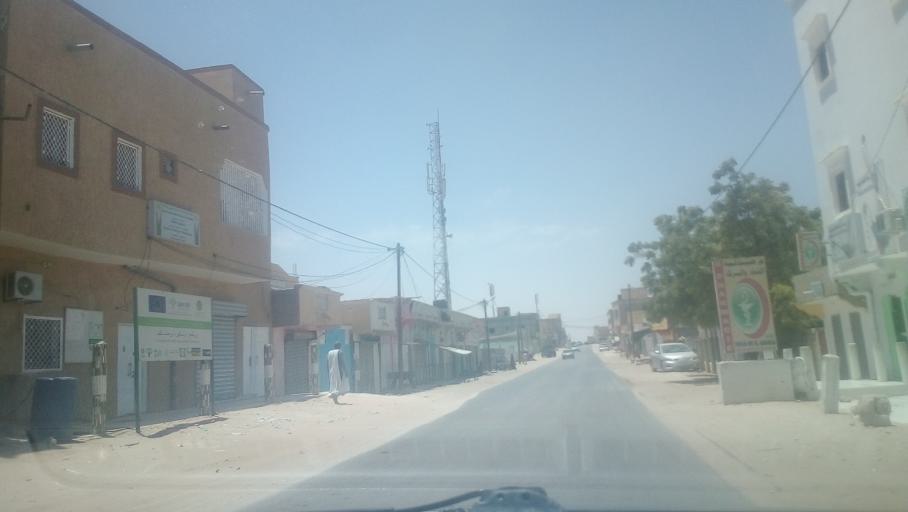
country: MR
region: Nouakchott
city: Nouakchott
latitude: 18.0629
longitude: -15.9598
